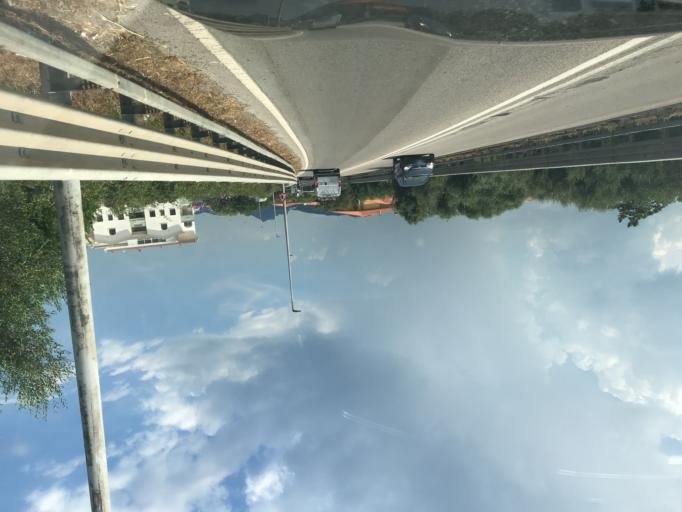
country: IT
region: Sardinia
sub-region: Provincia di Olbia-Tempio
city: Olbia
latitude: 40.9129
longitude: 9.5022
